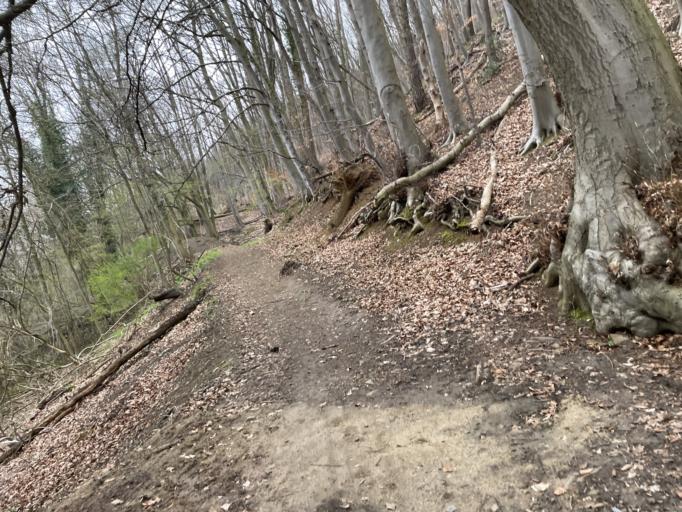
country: DE
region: North Rhine-Westphalia
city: Porta Westfalica
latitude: 52.2397
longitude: 8.9340
